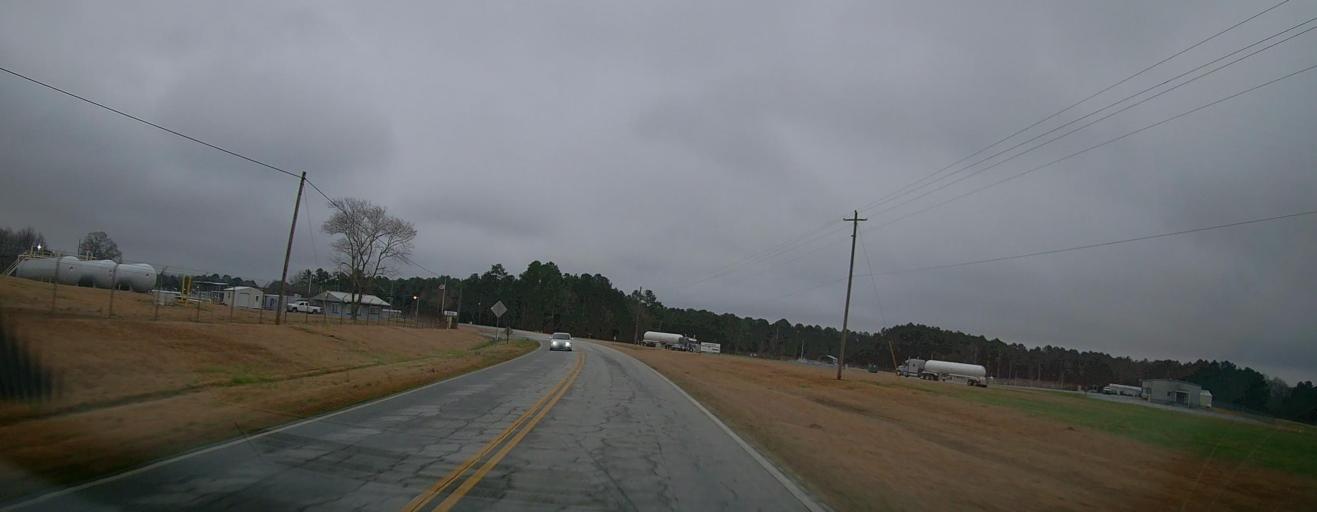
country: US
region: Georgia
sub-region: Spalding County
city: East Griffin
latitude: 33.1522
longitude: -84.2082
